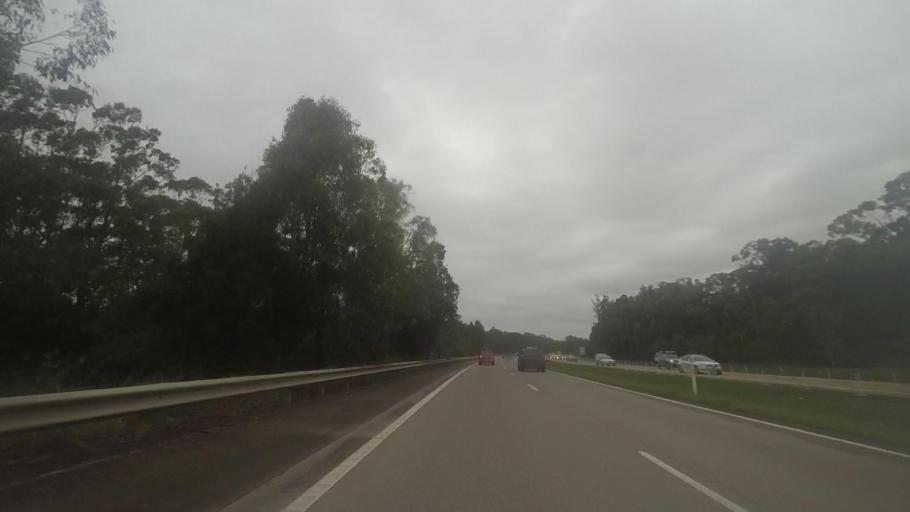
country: AU
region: New South Wales
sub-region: Port Stephens Shire
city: Medowie
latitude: -32.6932
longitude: 151.8087
